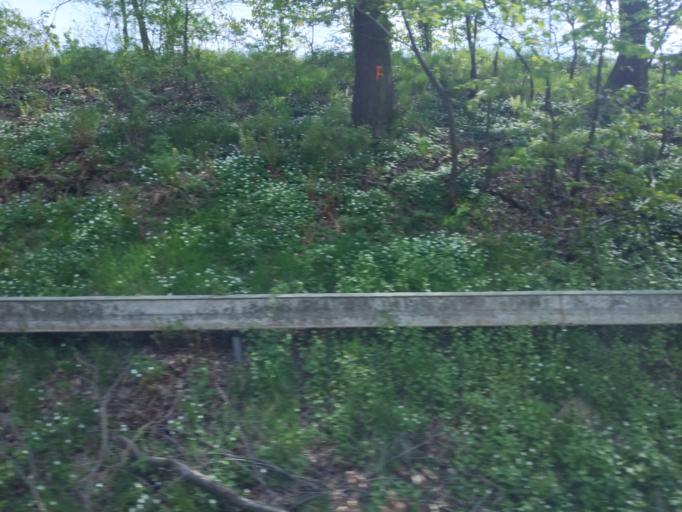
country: DE
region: Saxony
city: Demitz-Thumitz
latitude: 51.1434
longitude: 14.2340
